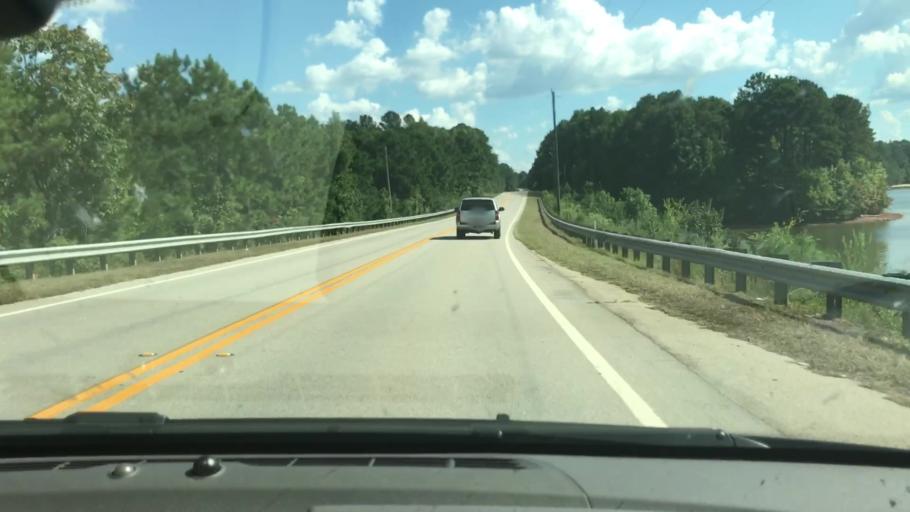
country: US
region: Georgia
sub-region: Troup County
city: La Grange
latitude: 33.0958
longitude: -85.0601
